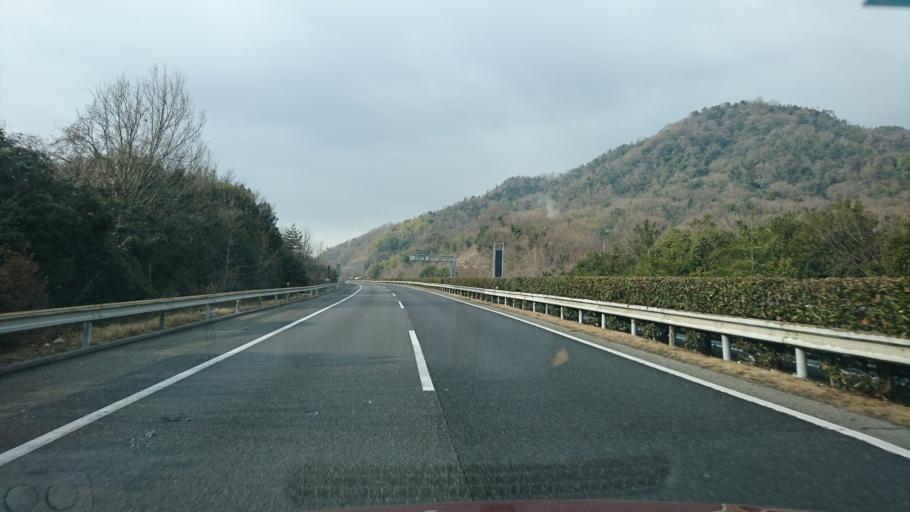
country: JP
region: Okayama
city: Kamogatacho-kamogata
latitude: 34.5671
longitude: 133.6302
